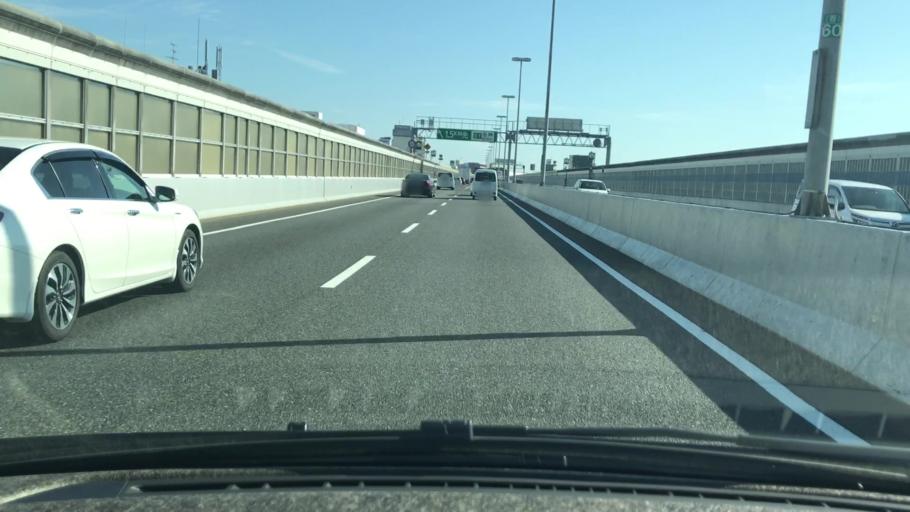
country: JP
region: Hyogo
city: Nishinomiya-hama
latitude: 34.7337
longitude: 135.3375
